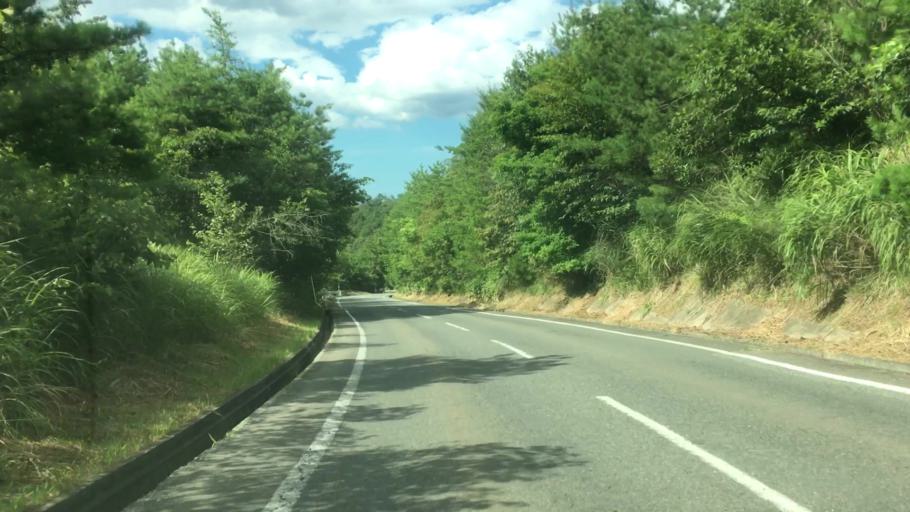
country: JP
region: Hyogo
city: Toyooka
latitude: 35.5194
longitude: 134.7910
